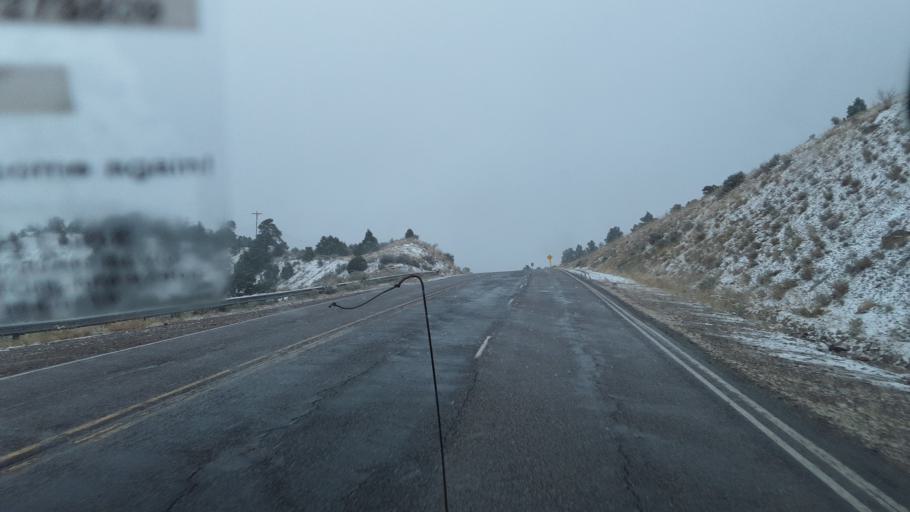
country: US
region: New Mexico
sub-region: Rio Arriba County
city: Tierra Amarilla
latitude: 36.6646
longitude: -106.5573
